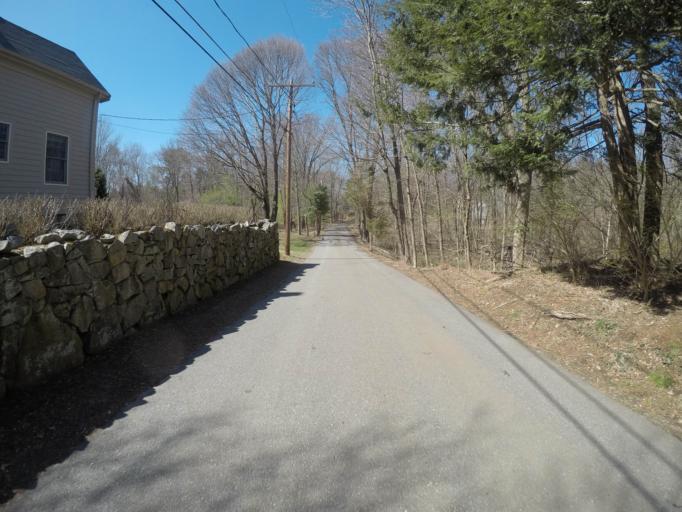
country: US
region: Massachusetts
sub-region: Norfolk County
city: Stoughton
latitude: 42.0734
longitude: -71.1024
